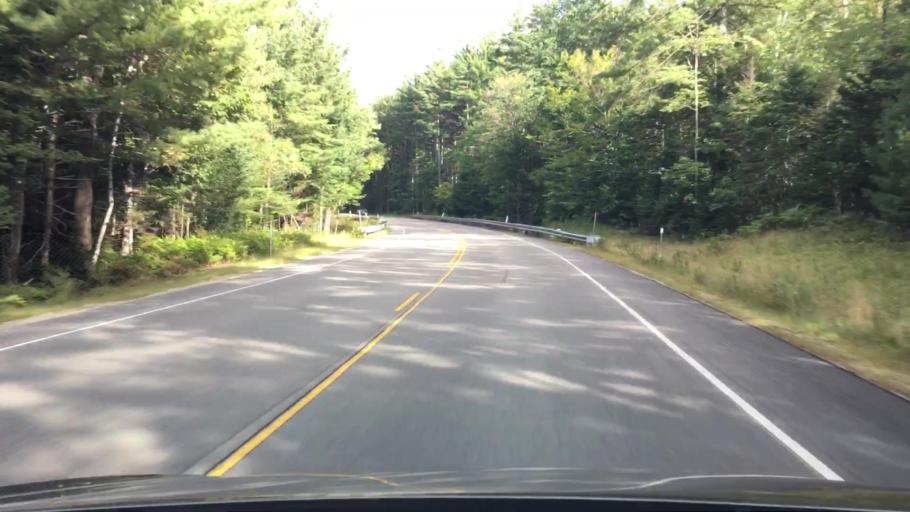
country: US
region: New Hampshire
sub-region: Carroll County
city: Tamworth
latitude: 43.9891
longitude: -71.3165
